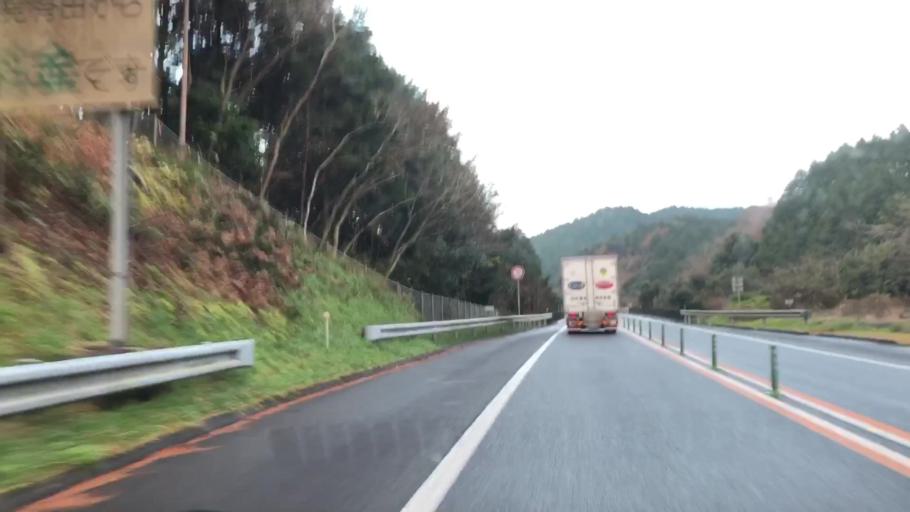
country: JP
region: Saga Prefecture
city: Ureshinomachi-shimojuku
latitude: 33.1570
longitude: 129.9156
